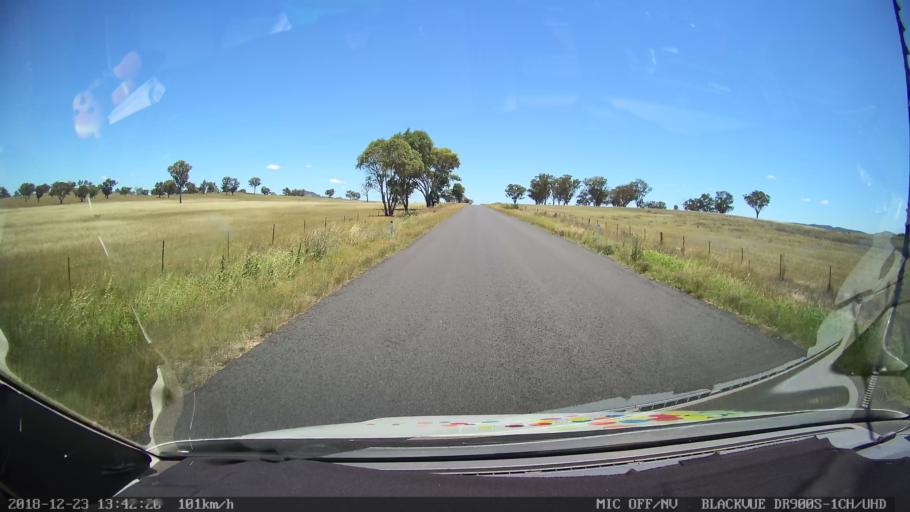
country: AU
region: New South Wales
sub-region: Armidale Dumaresq
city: Armidale
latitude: -30.4759
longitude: 151.1637
